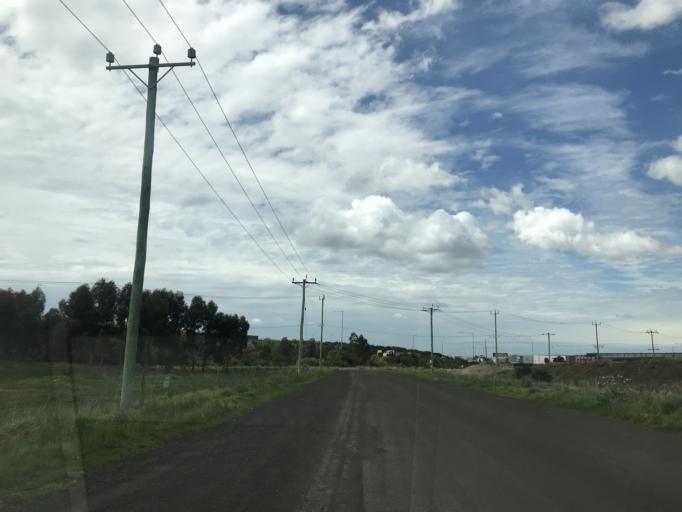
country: AU
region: Victoria
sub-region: Brimbank
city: Derrimut
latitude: -37.7958
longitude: 144.7497
